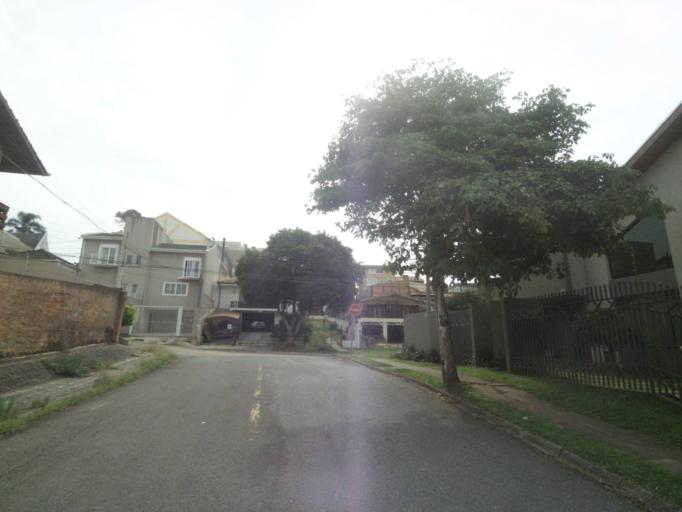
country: BR
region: Parana
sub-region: Curitiba
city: Curitiba
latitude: -25.4082
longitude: -49.2960
